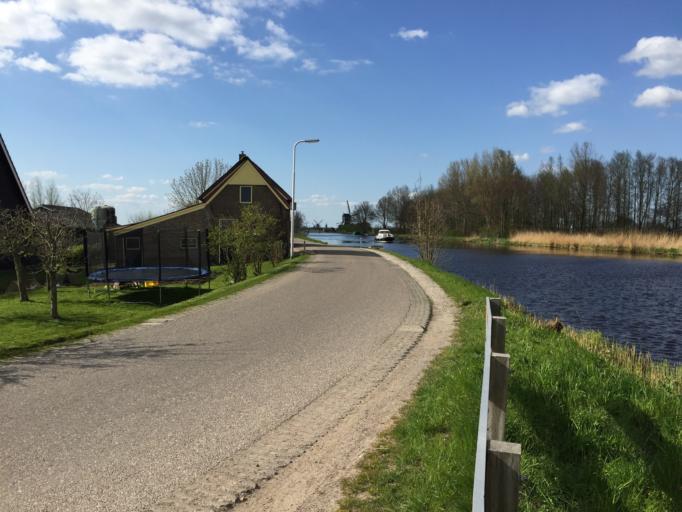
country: NL
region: South Holland
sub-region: Molenwaard
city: Liesveld
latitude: 51.9021
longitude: 4.8432
